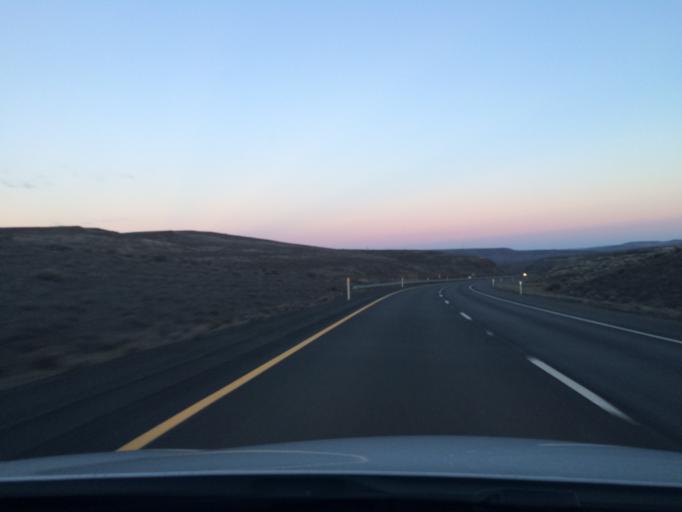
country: US
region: Washington
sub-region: Grant County
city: Mattawa
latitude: 46.9385
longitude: -120.0278
